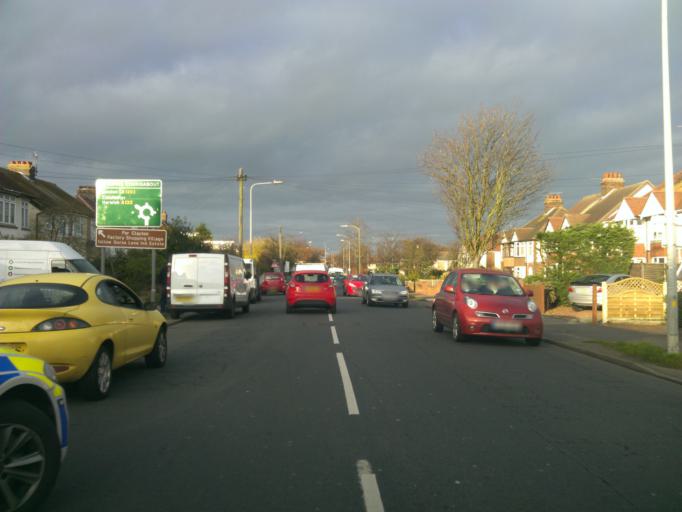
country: GB
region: England
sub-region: Essex
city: Clacton-on-Sea
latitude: 51.8022
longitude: 1.1481
